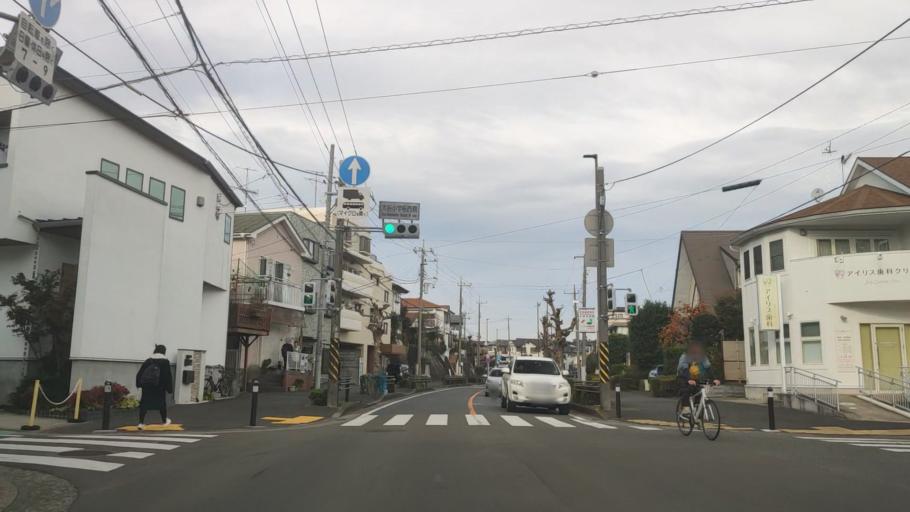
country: JP
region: Kanagawa
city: Atsugi
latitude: 35.4401
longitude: 139.4025
